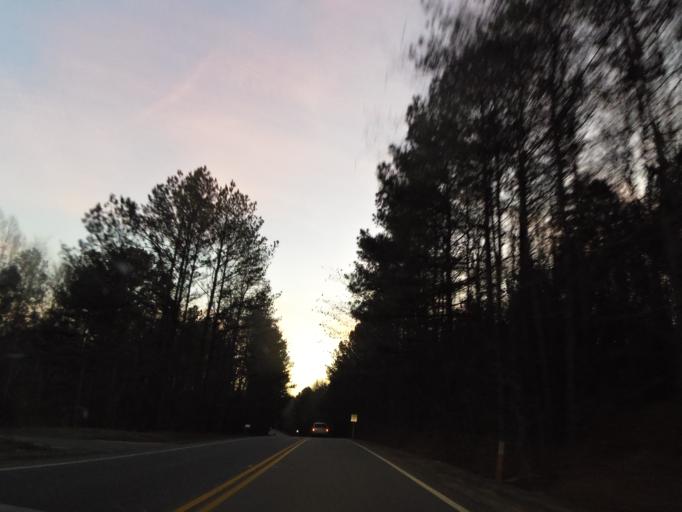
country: US
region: Georgia
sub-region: Whitfield County
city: Varnell
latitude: 34.9872
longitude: -84.9310
